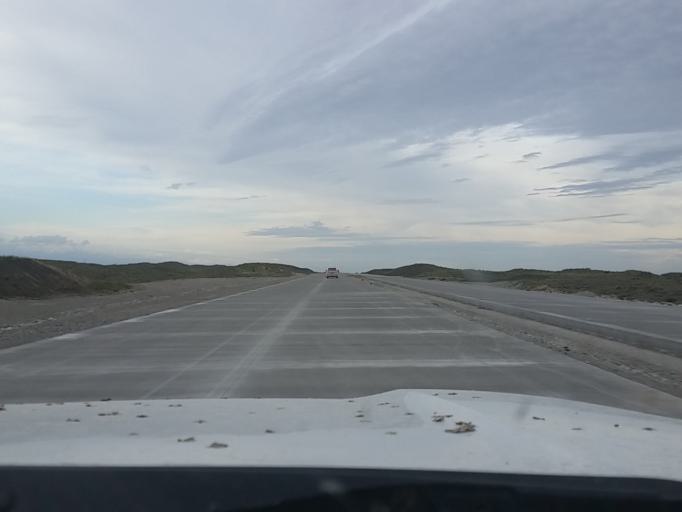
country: KZ
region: Almaty Oblysy
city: Zharkent
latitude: 44.1744
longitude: 80.3170
